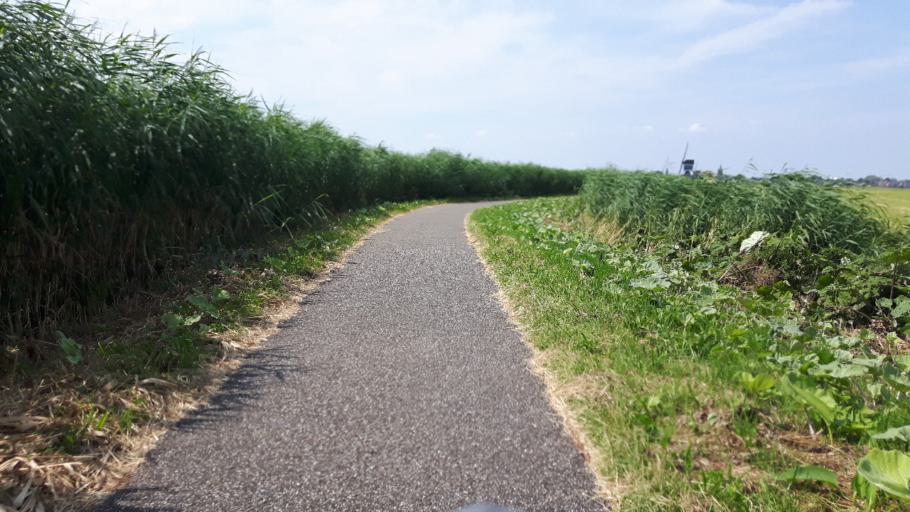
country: NL
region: South Holland
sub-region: Molenwaard
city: Liesveld
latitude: 51.9119
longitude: 4.8308
